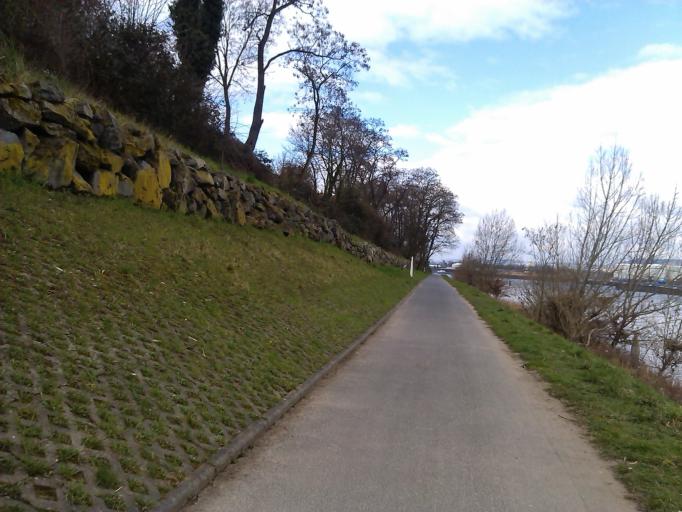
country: DE
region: Rheinland-Pfalz
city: Sankt Sebastian
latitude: 50.4098
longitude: 7.5686
